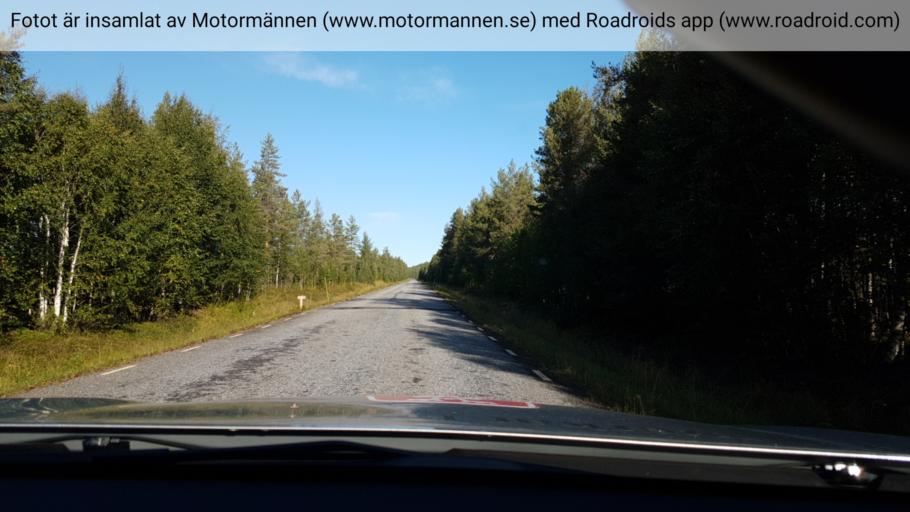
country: SE
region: Vaesterbotten
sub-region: Lycksele Kommun
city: Lycksele
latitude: 64.4725
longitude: 18.8174
